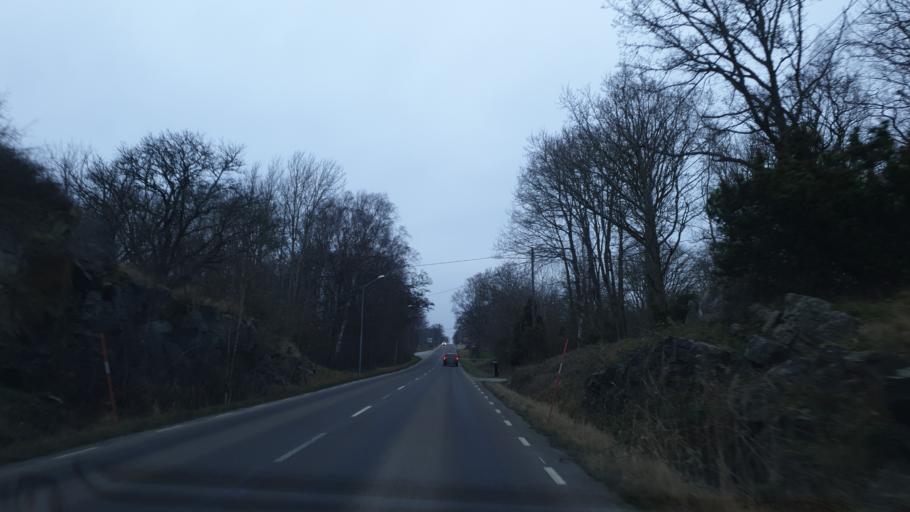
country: SE
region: Blekinge
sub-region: Karlskrona Kommun
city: Sturko
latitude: 56.1217
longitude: 15.7351
